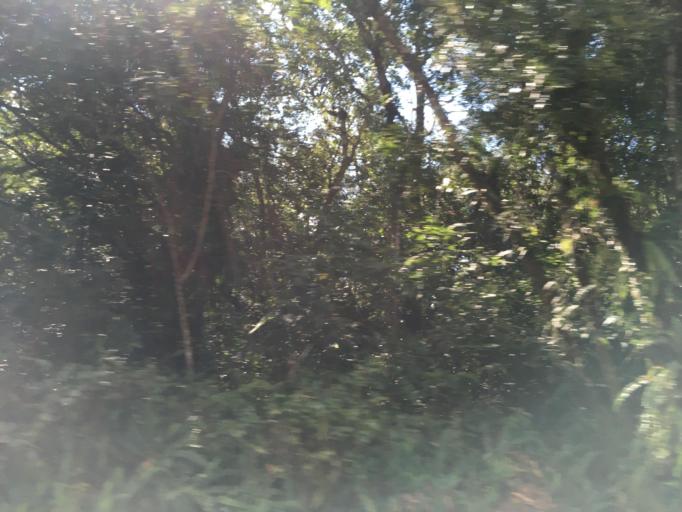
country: TW
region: Taiwan
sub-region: Yilan
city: Yilan
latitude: 24.7565
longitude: 121.5936
